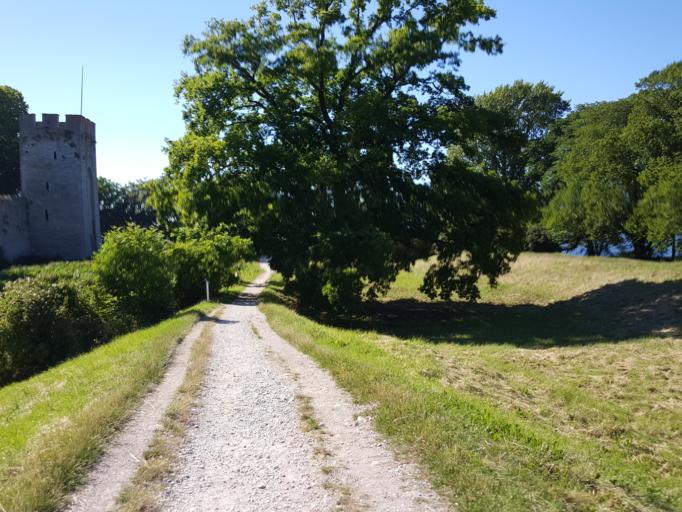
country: SE
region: Gotland
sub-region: Gotland
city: Visby
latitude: 57.6465
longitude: 18.2980
